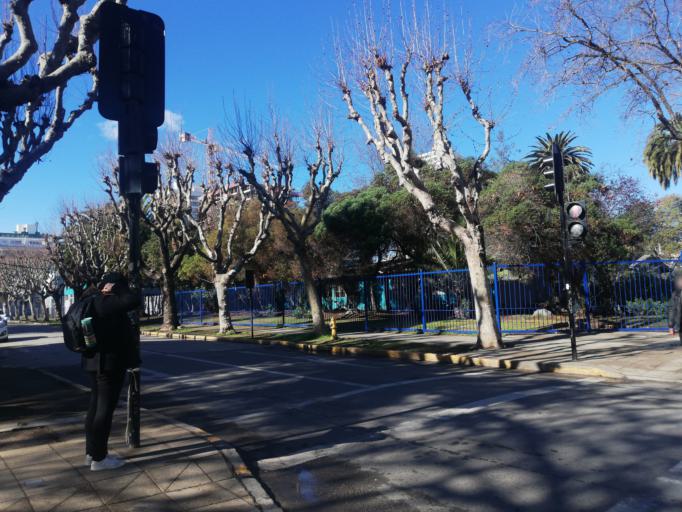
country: CL
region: Valparaiso
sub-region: Provincia de Valparaiso
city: Vina del Mar
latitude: -33.0205
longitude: -71.5510
